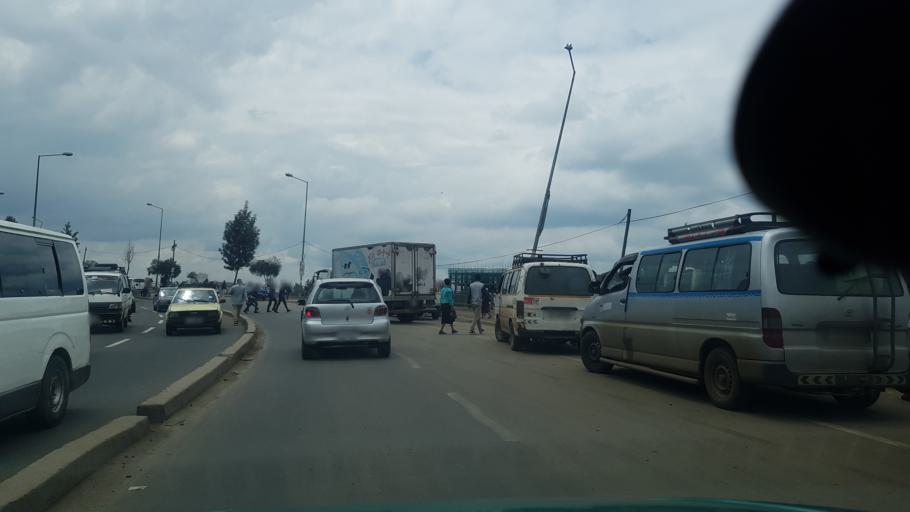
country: ET
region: Adis Abeba
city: Addis Ababa
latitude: 9.0205
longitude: 38.8031
